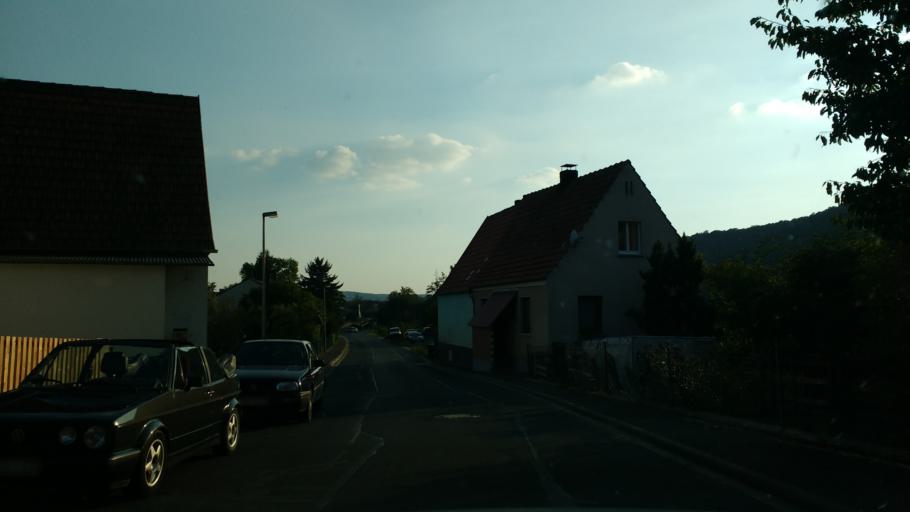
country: DE
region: Bavaria
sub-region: Regierungsbezirk Unterfranken
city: Elfershausen
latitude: 50.1478
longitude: 9.9596
